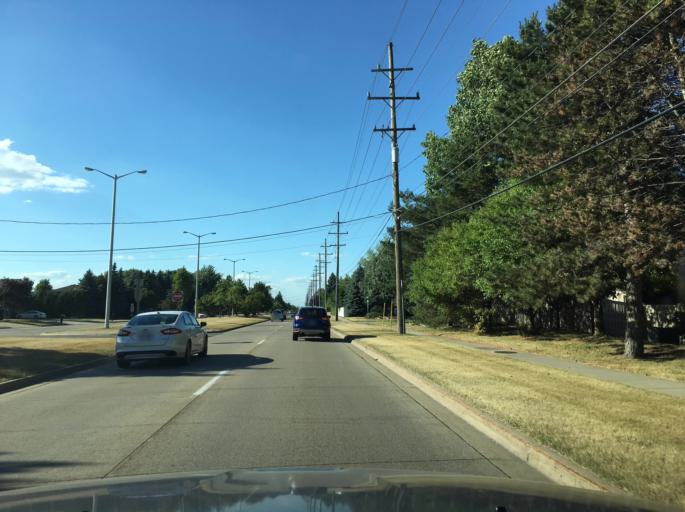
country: US
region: Michigan
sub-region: Macomb County
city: Sterling Heights
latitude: 42.6036
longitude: -82.9917
